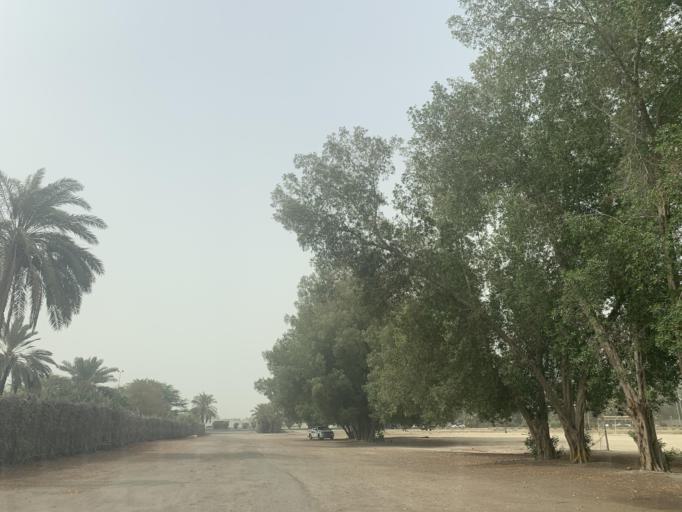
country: BH
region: Manama
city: Jidd Hafs
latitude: 26.2228
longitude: 50.5534
